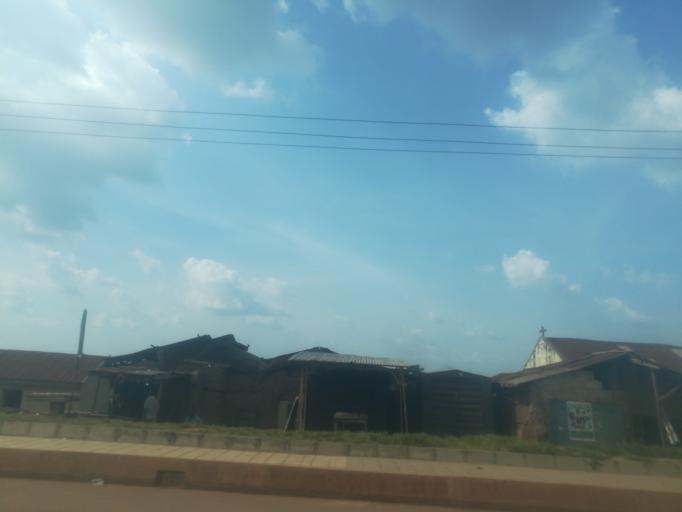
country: NG
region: Ogun
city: Abeokuta
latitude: 7.1640
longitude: 3.3338
